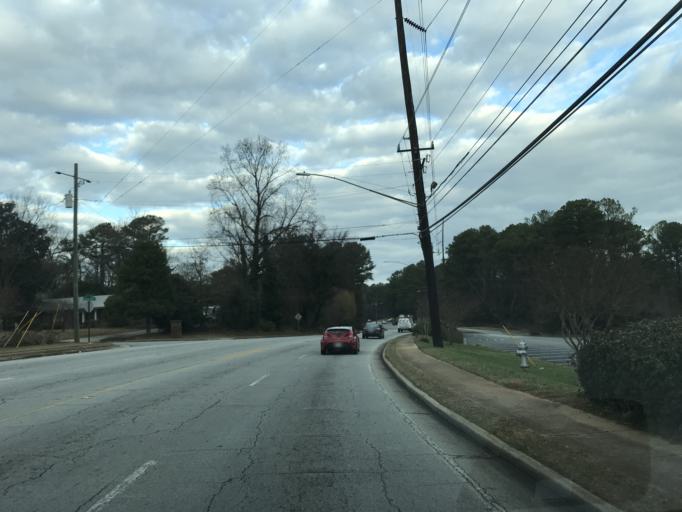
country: US
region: Georgia
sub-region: DeKalb County
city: Tucker
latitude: 33.8813
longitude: -84.2310
